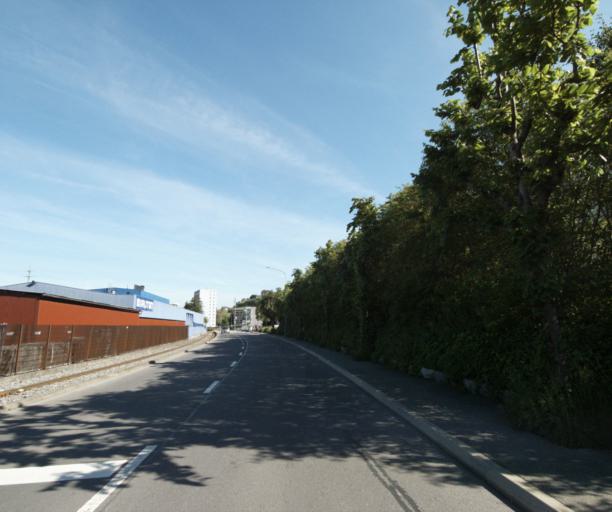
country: CH
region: Vaud
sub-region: Aigle District
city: Villeneuve
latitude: 46.3930
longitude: 6.9354
